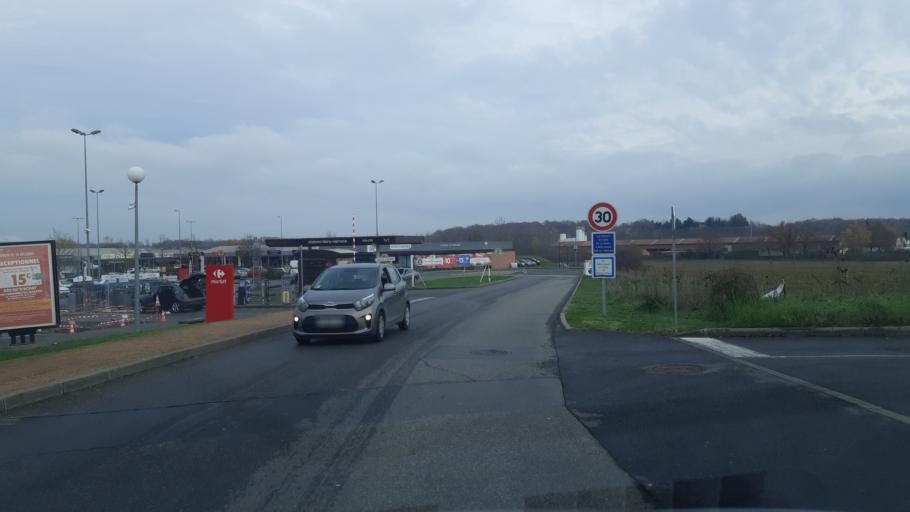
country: FR
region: Midi-Pyrenees
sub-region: Departement de la Haute-Garonne
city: Pibrac
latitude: 43.6078
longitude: 1.2841
